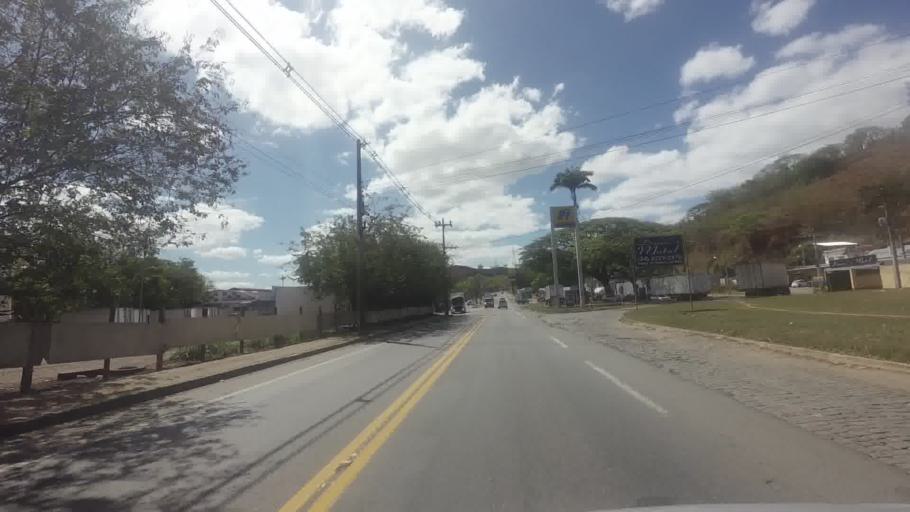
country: BR
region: Minas Gerais
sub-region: Alem Paraiba
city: Alem Paraiba
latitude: -21.8774
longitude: -42.6734
